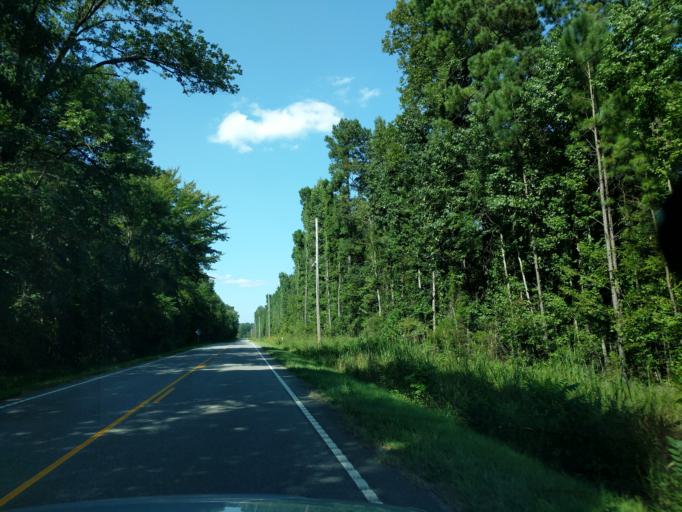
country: US
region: South Carolina
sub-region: Newberry County
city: Prosperity
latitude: 34.0683
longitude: -81.5606
